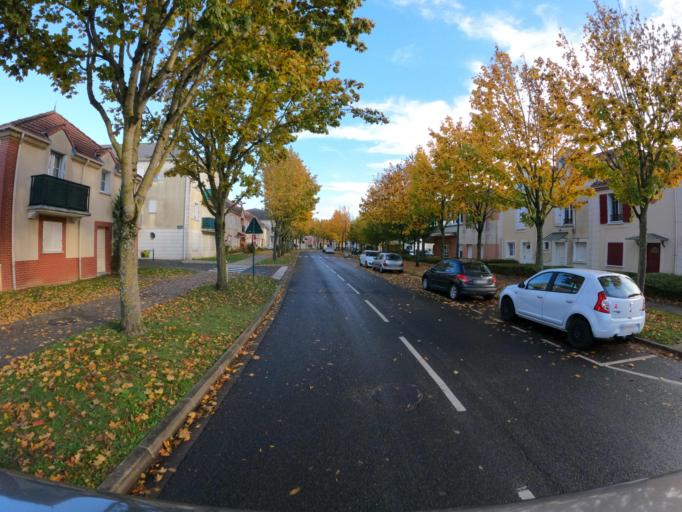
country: FR
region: Ile-de-France
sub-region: Departement de Seine-et-Marne
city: Bailly-Romainvilliers
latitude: 48.8490
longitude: 2.8178
